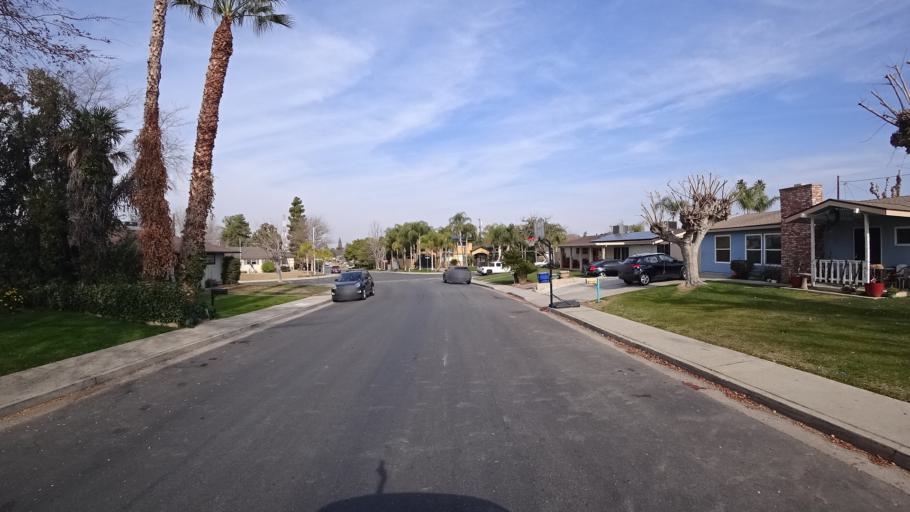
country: US
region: California
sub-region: Kern County
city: Oildale
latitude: 35.4068
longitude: -118.9617
